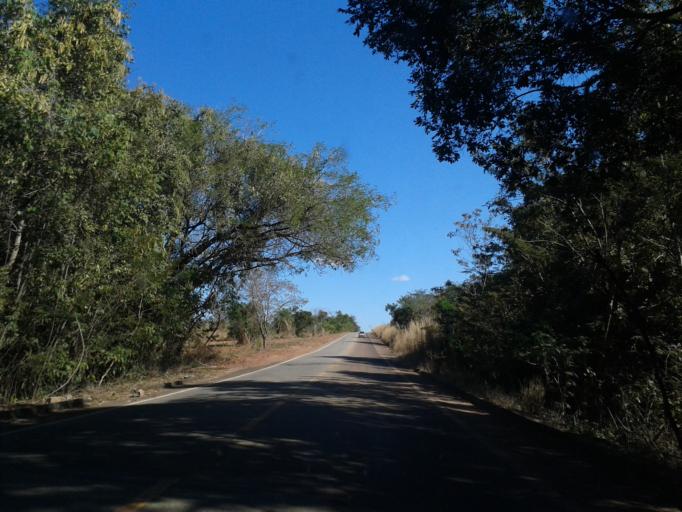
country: BR
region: Goias
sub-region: Mozarlandia
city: Mozarlandia
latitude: -14.4068
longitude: -50.4452
